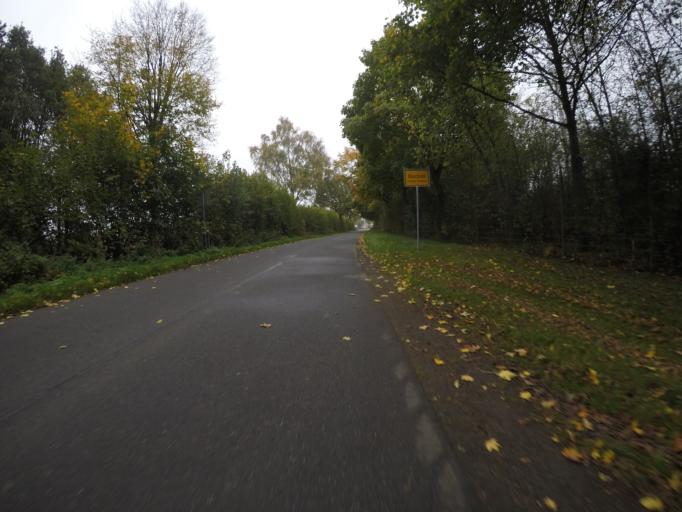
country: DE
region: North Rhine-Westphalia
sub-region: Regierungsbezirk Munster
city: Isselburg
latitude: 51.8170
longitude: 6.5372
